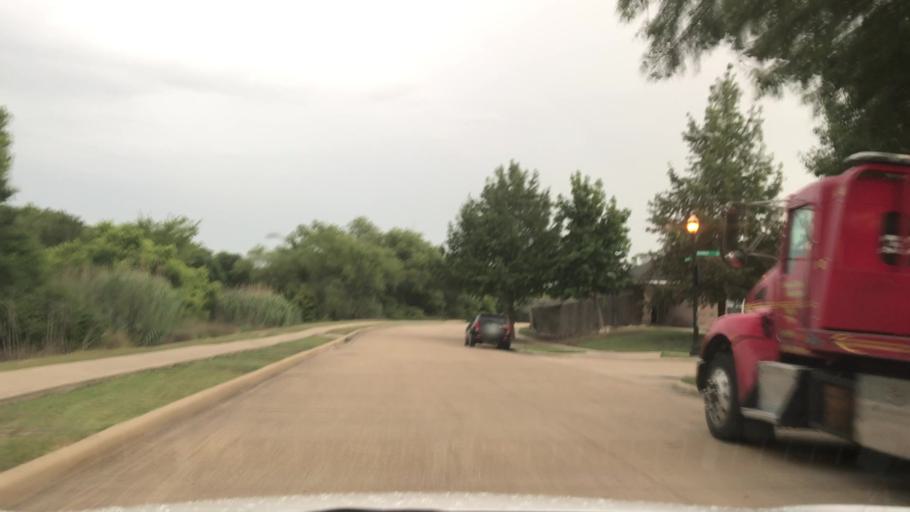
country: US
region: Texas
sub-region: Kaufman County
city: Forney
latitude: 32.7207
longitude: -96.5348
